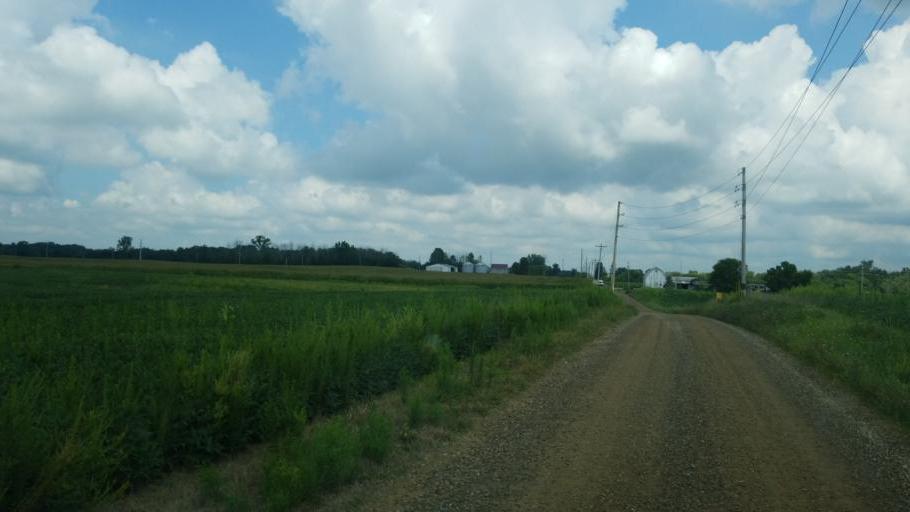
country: US
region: Ohio
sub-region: Knox County
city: Mount Vernon
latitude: 40.3327
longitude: -82.4859
